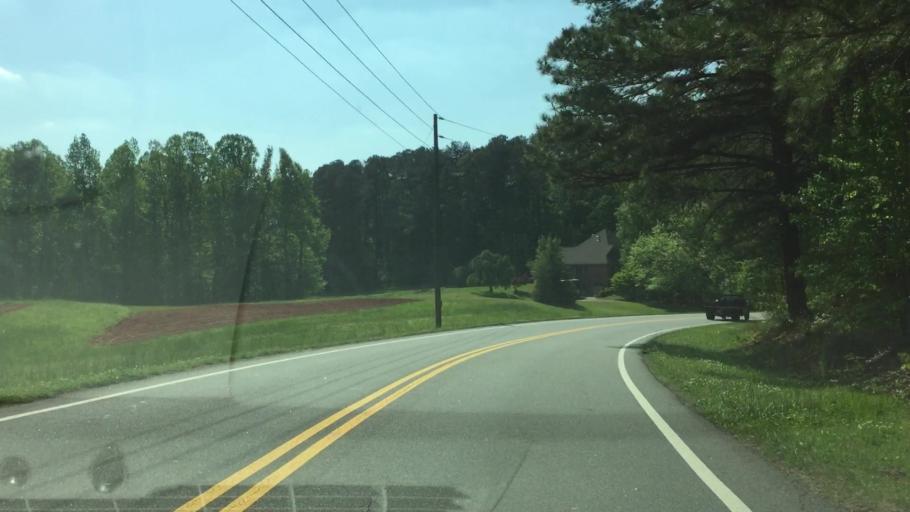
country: US
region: Georgia
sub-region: Fulton County
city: Milton
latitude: 34.1548
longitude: -84.2592
